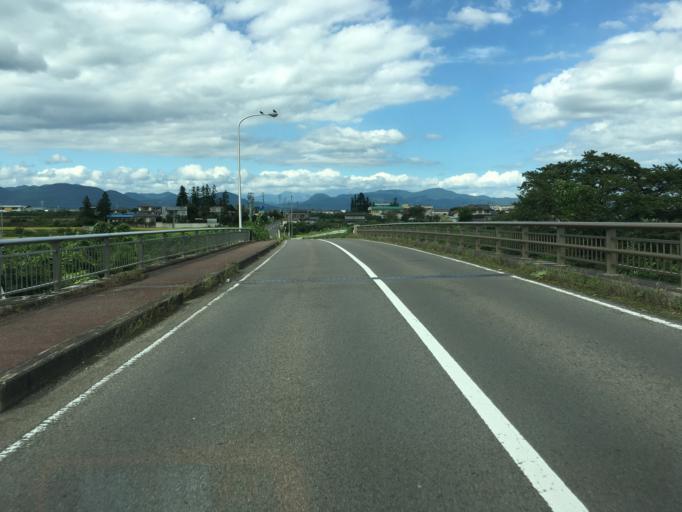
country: JP
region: Fukushima
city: Fukushima-shi
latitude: 37.7541
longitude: 140.4191
